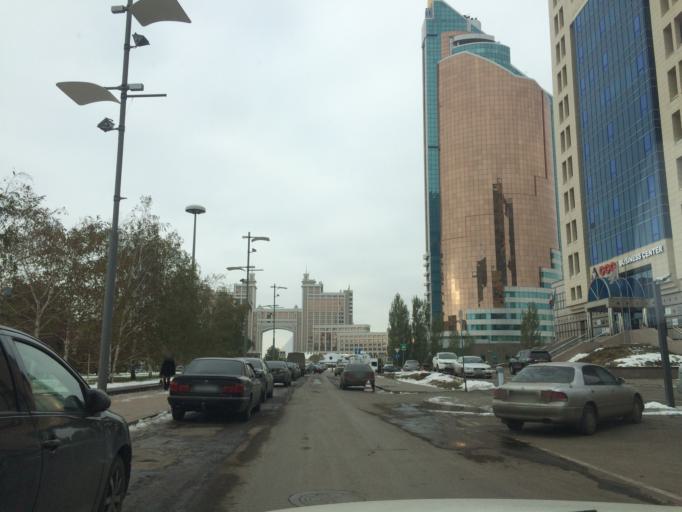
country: KZ
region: Astana Qalasy
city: Astana
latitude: 51.1305
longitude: 71.4191
